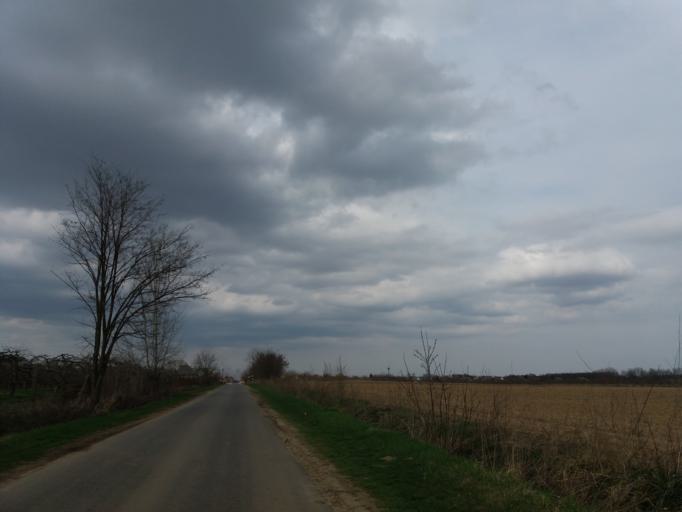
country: HU
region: Szabolcs-Szatmar-Bereg
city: Nyirtass
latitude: 48.0974
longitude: 22.0292
